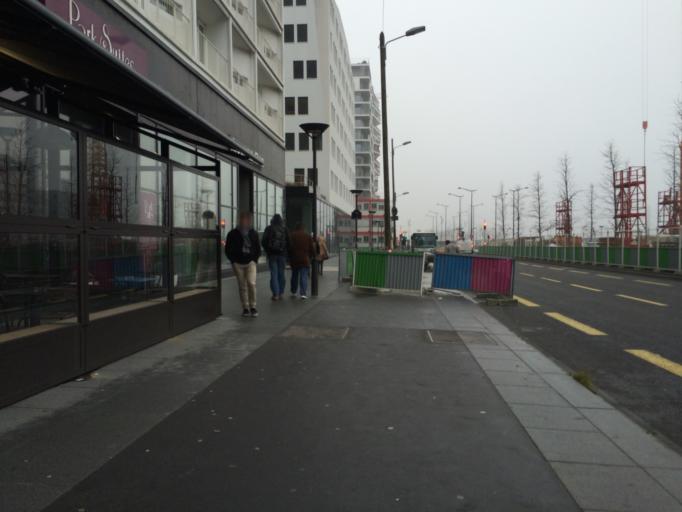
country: FR
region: Ile-de-France
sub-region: Departement du Val-de-Marne
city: Ivry-sur-Seine
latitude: 48.8279
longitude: 2.3795
